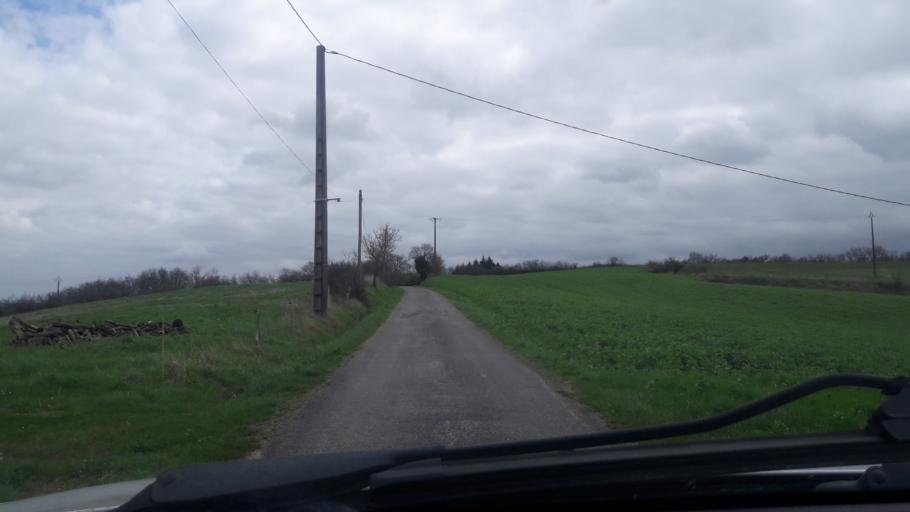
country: FR
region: Midi-Pyrenees
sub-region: Departement de l'Ariege
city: Lezat-sur-Leze
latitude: 43.1930
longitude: 1.3274
